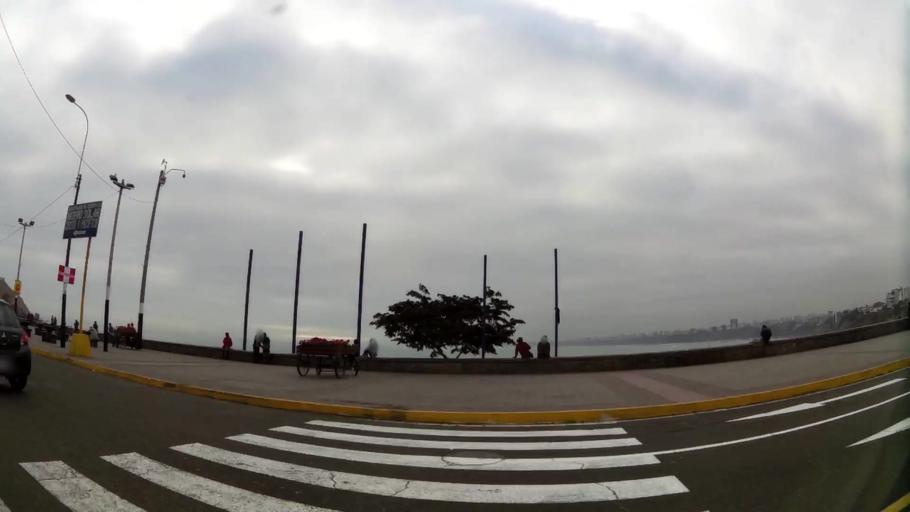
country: PE
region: Lima
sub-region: Lima
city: Surco
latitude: -12.1662
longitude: -77.0268
